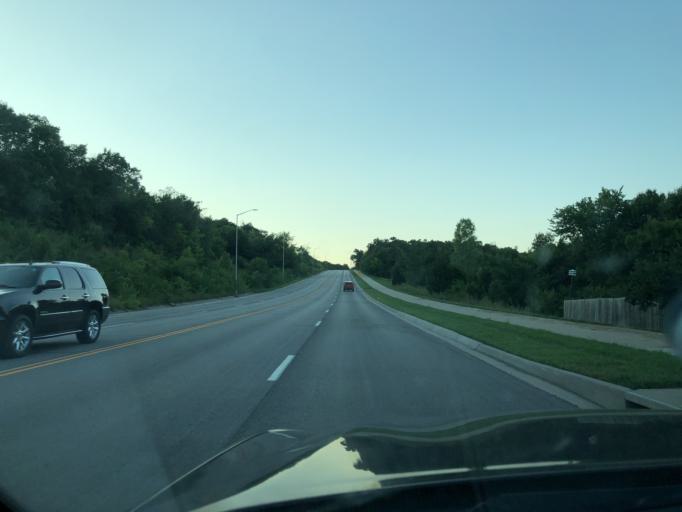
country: US
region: Kansas
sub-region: Leavenworth County
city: Leavenworth
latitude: 39.2944
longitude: -94.9505
